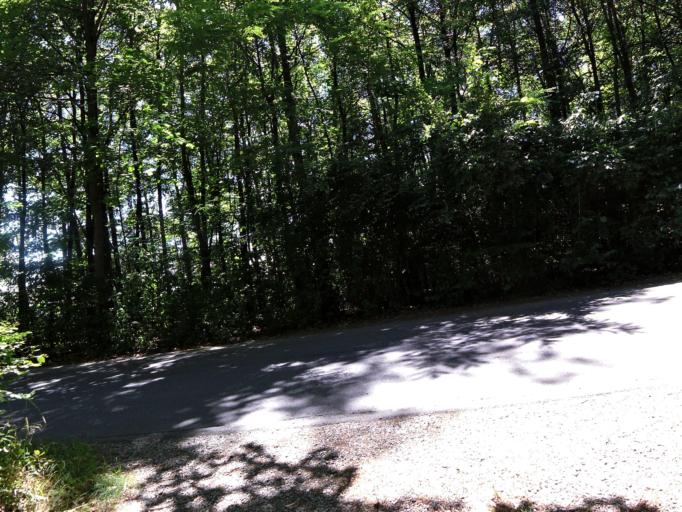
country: DE
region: Bavaria
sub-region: Regierungsbezirk Unterfranken
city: Hochberg
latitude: 49.7821
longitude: 9.9114
